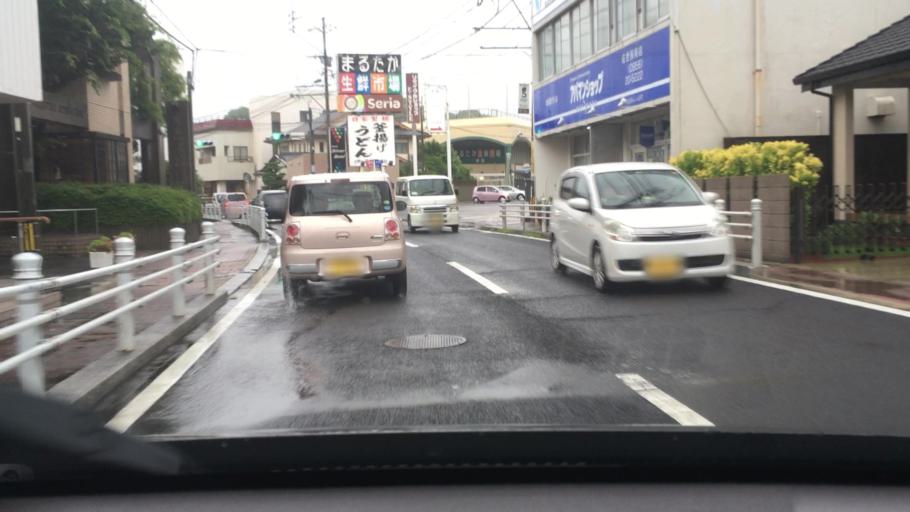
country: JP
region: Nagasaki
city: Sasebo
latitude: 33.1363
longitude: 129.7984
